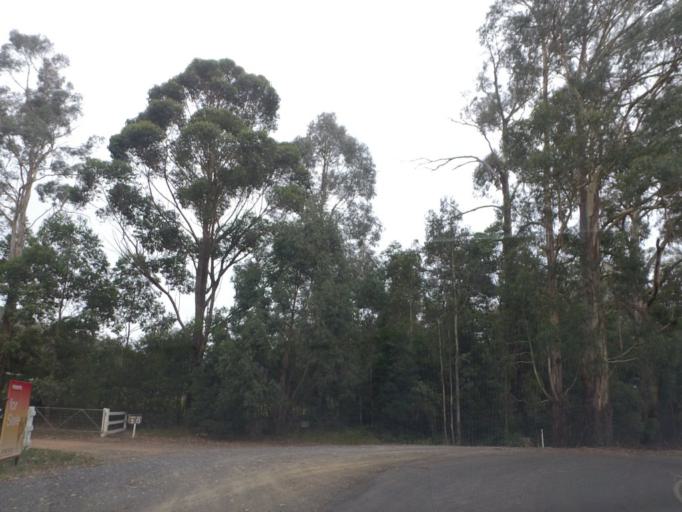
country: AU
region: Victoria
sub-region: Murrindindi
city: Alexandra
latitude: -37.3740
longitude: 145.5415
